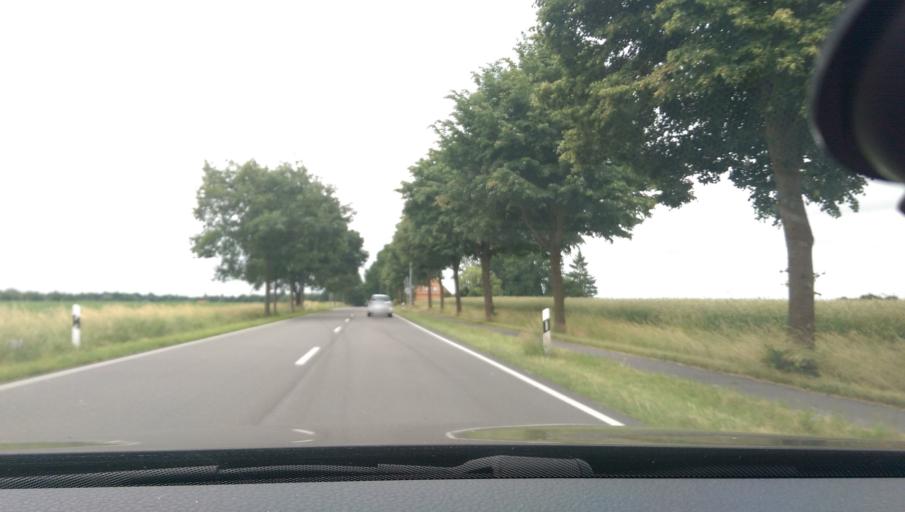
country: DE
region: Lower Saxony
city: Botersen
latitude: 53.1742
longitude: 9.2938
